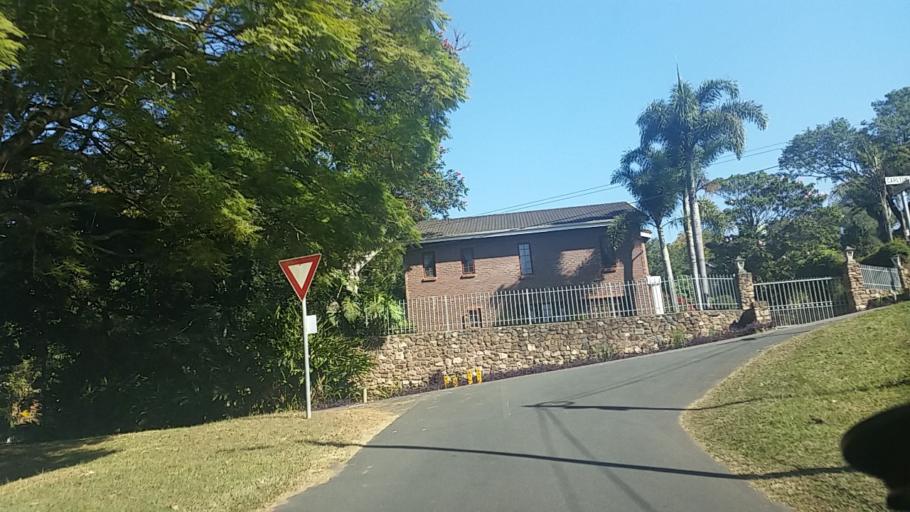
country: ZA
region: KwaZulu-Natal
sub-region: eThekwini Metropolitan Municipality
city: Berea
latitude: -29.8514
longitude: 30.9051
